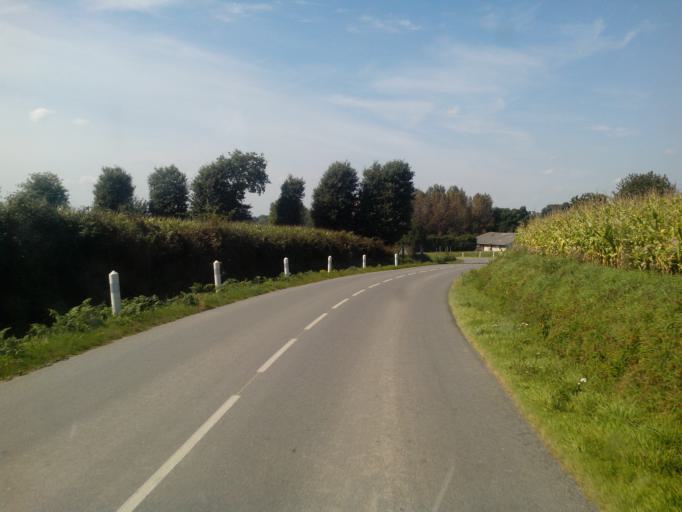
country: FR
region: Brittany
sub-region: Departement d'Ille-et-Vilaine
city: Gael
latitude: 48.1300
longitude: -2.1982
